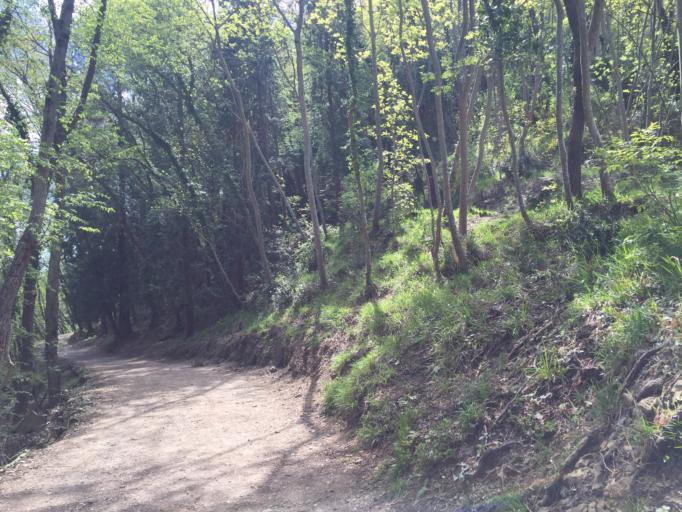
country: IT
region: Liguria
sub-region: Provincia di Genova
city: Camogli
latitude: 44.3301
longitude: 9.1708
